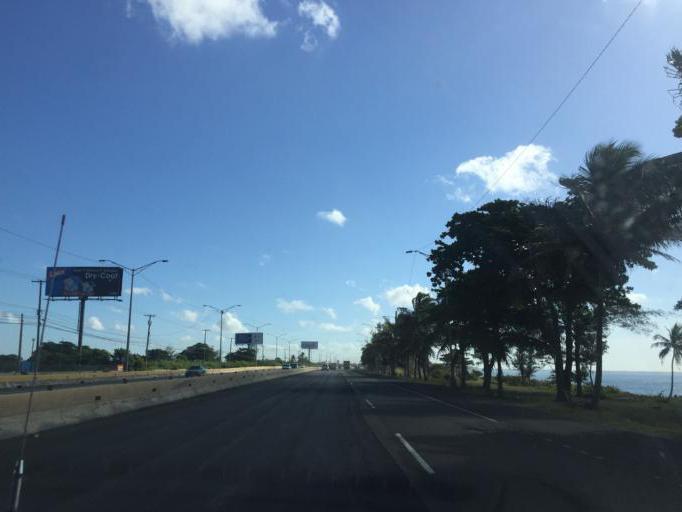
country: DO
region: Santo Domingo
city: Guerra
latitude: 18.4636
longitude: -69.7476
